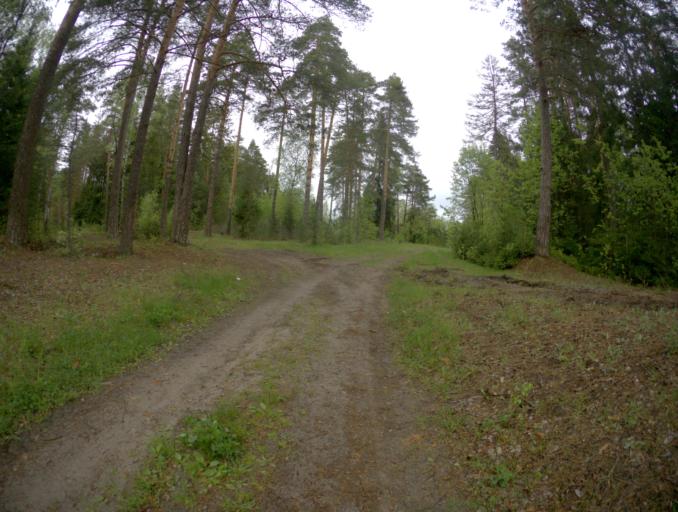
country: RU
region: Vladimir
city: Kurlovo
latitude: 55.4360
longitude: 40.6136
